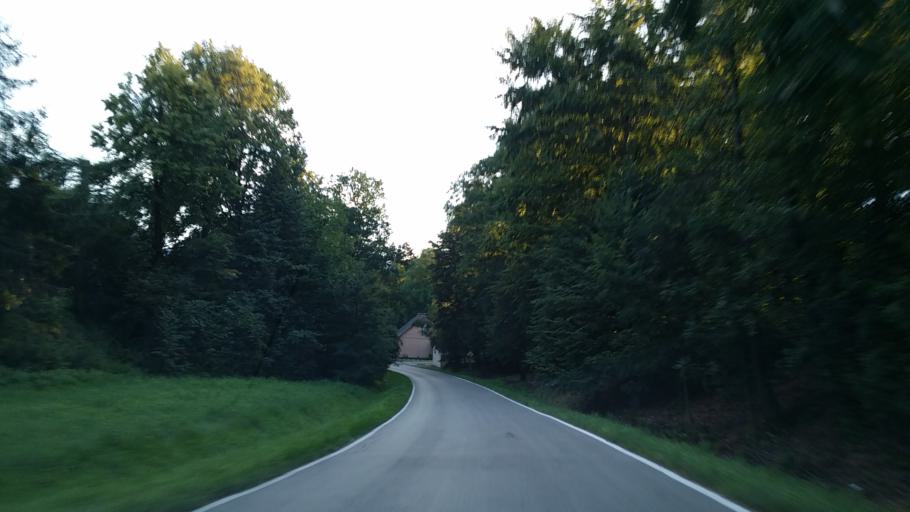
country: PL
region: Lesser Poland Voivodeship
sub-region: Powiat oswiecimski
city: Malec
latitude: 49.9235
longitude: 19.2466
